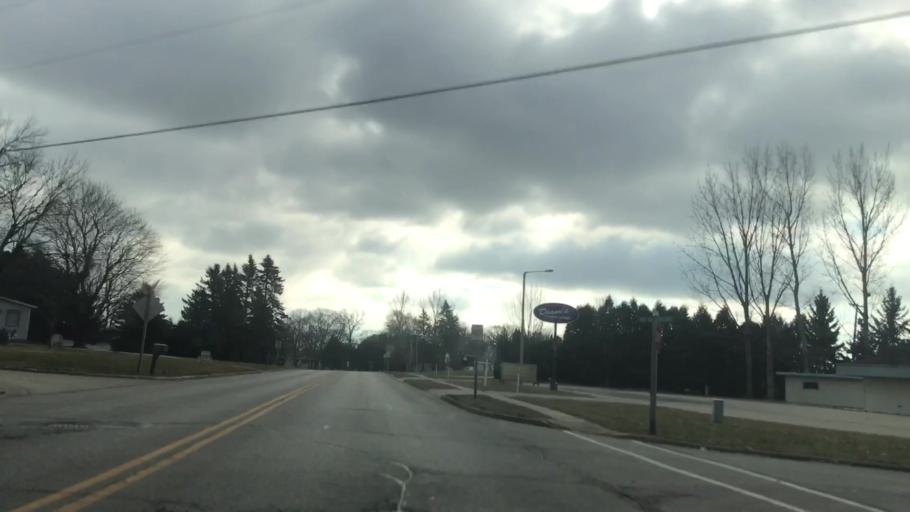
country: US
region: Wisconsin
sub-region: Dodge County
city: Horicon
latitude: 43.4481
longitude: -88.6201
